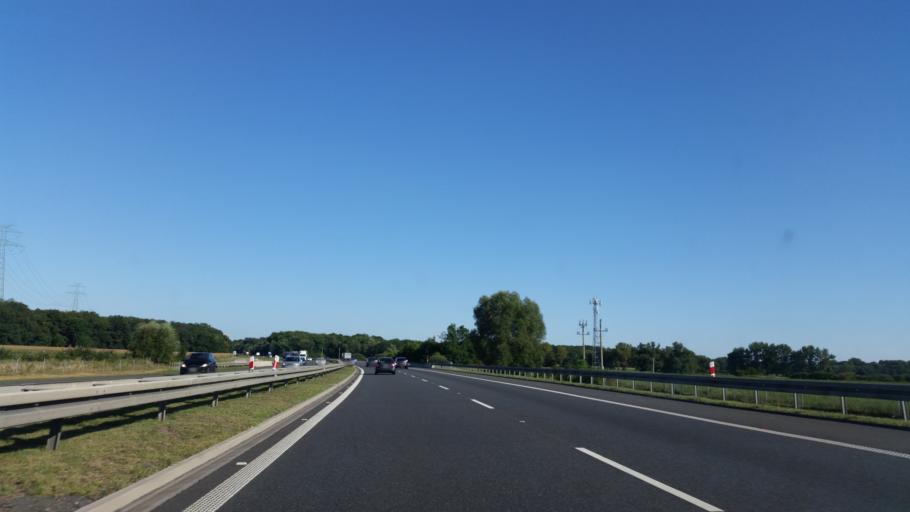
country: PL
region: Lower Silesian Voivodeship
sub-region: Powiat strzelinski
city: Wiazow
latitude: 50.8523
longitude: 17.2333
